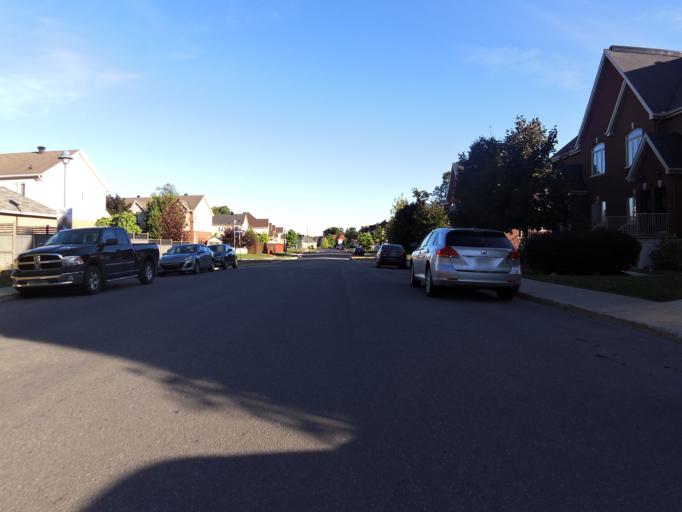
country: CA
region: Ontario
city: Bells Corners
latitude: 45.4225
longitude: -75.8483
